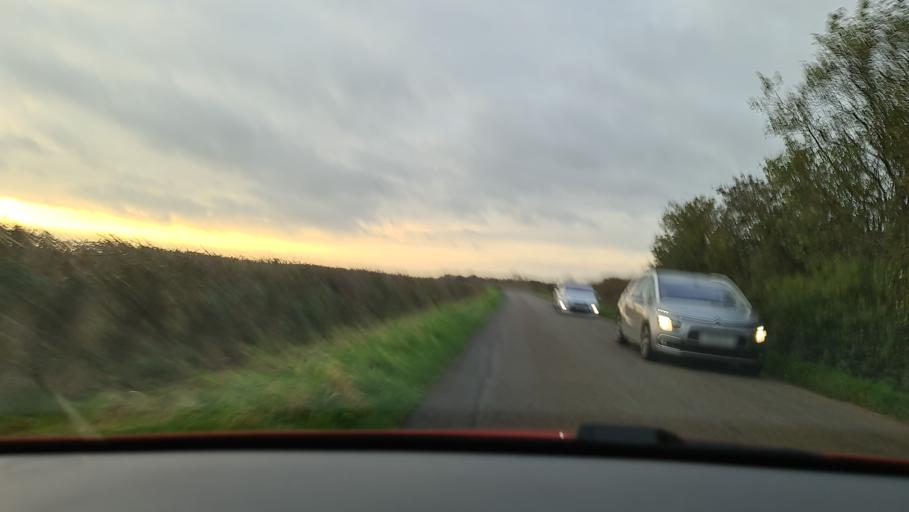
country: GB
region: England
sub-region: Oxfordshire
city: Somerton
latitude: 51.9140
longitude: -1.2752
